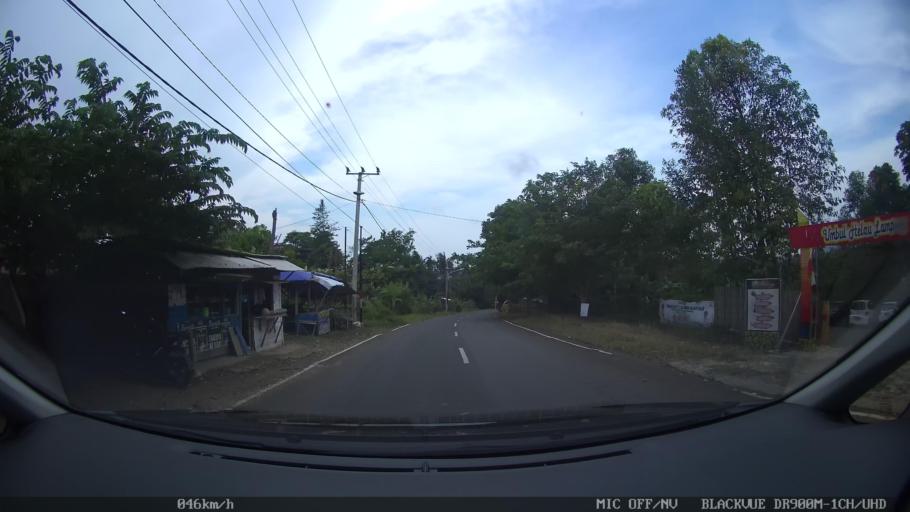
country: ID
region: Lampung
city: Bandarlampung
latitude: -5.4215
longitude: 105.1923
